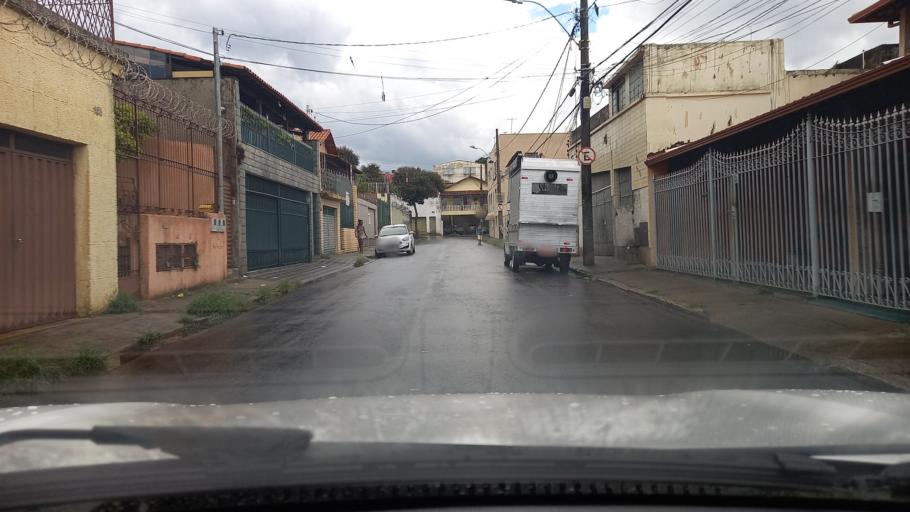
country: BR
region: Minas Gerais
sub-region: Belo Horizonte
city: Belo Horizonte
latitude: -19.9050
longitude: -43.9522
